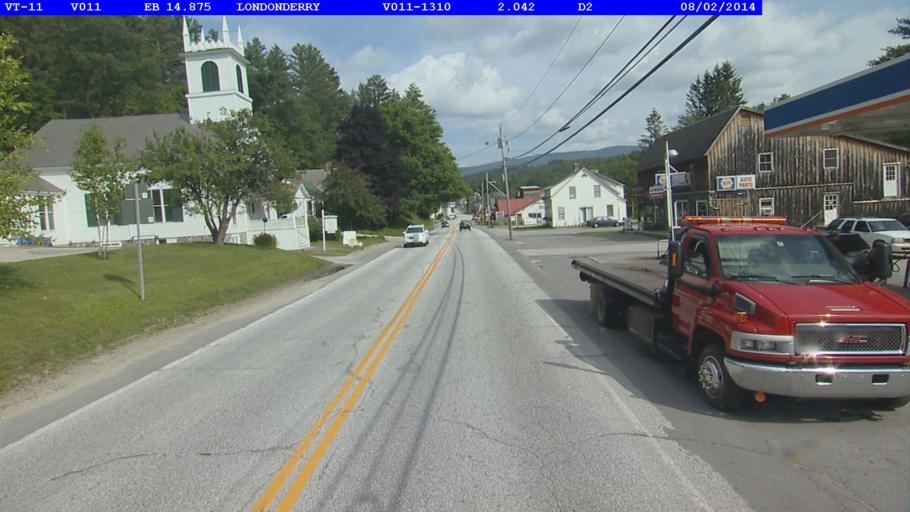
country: US
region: Vermont
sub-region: Windsor County
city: Chester
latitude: 43.2291
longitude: -72.8129
